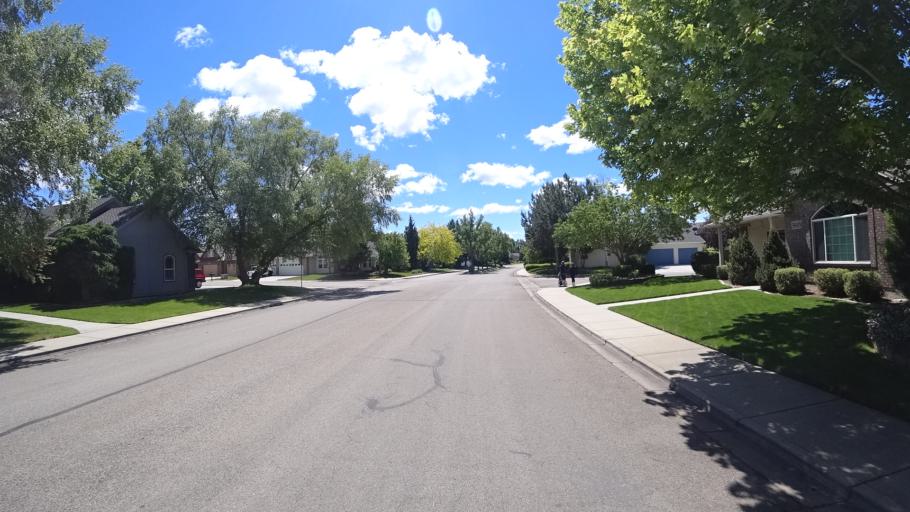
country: US
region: Idaho
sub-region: Ada County
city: Eagle
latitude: 43.6509
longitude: -116.3410
